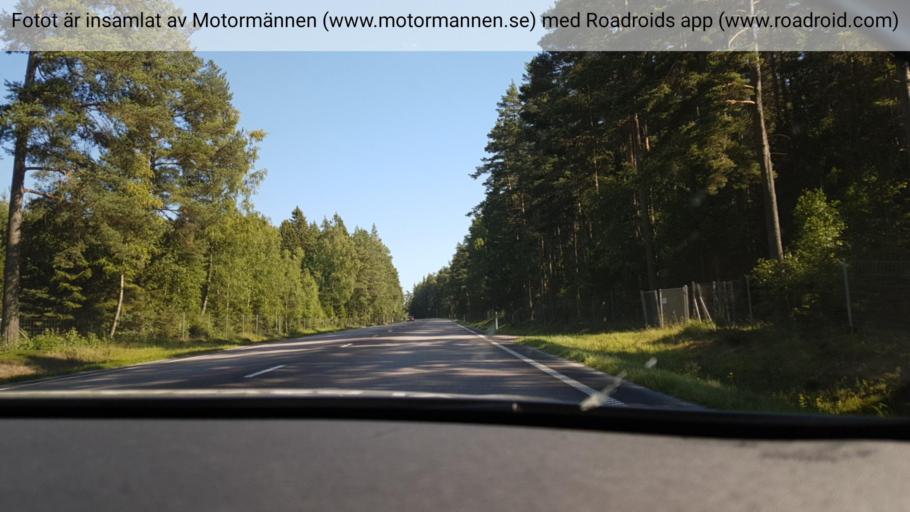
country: SE
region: Vaestra Goetaland
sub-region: Lidkopings Kommun
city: Vinninga
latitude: 58.4720
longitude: 13.2100
